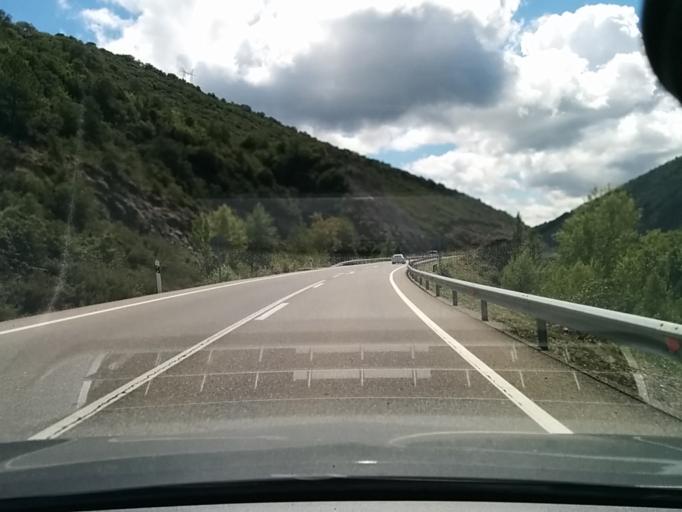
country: ES
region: Aragon
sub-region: Provincia de Huesca
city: Boltana
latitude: 42.4561
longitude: 0.0535
